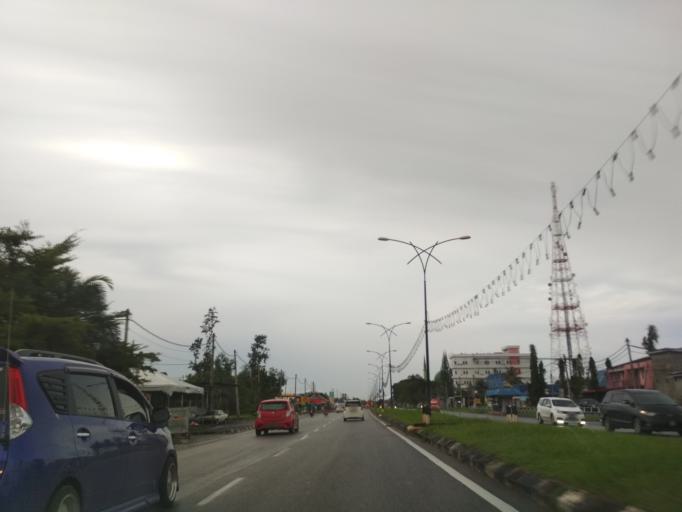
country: MY
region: Perlis
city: Kangar
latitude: 6.4490
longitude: 100.2054
